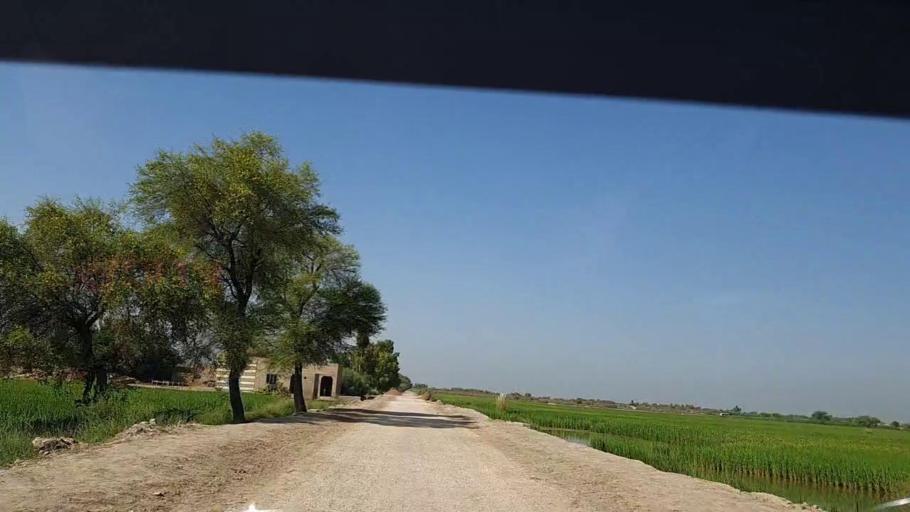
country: PK
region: Sindh
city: Tangwani
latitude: 28.3313
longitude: 69.0723
